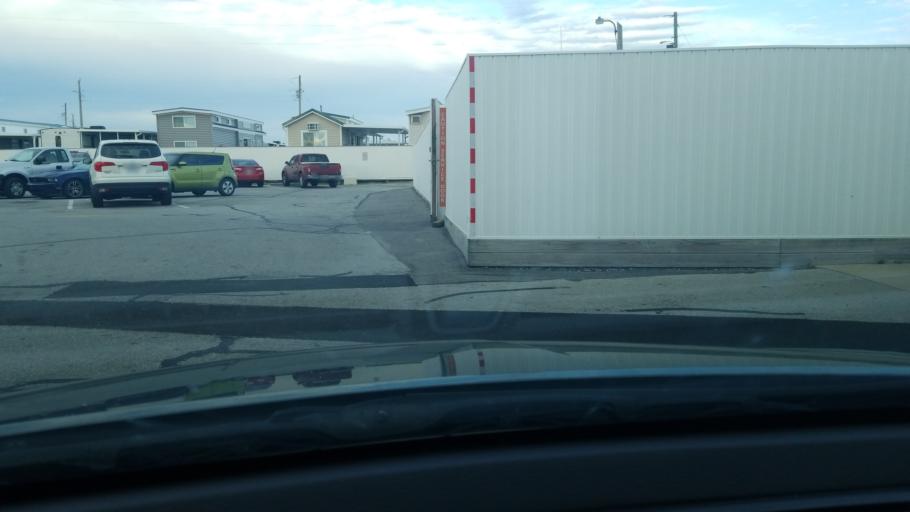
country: US
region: North Carolina
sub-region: Carteret County
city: Cape Carteret
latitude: 34.6609
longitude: -77.0340
